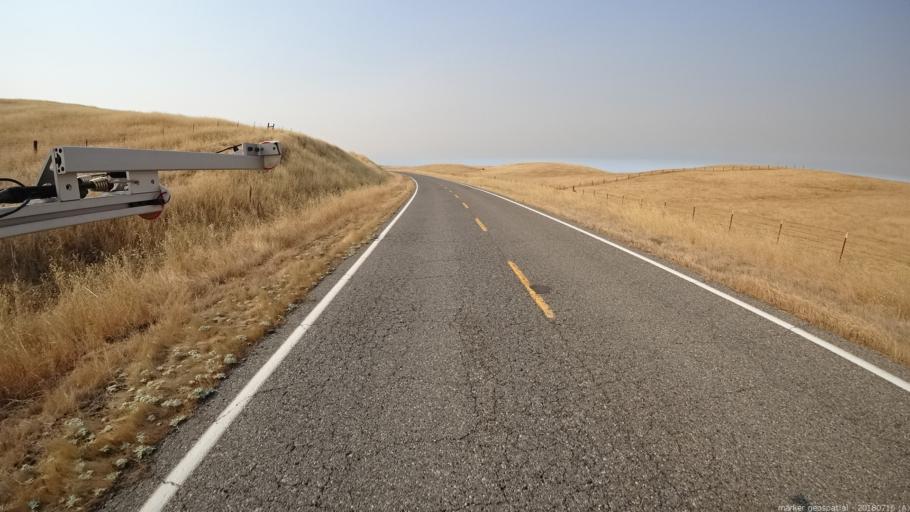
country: US
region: California
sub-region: Madera County
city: Madera Acres
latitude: 37.1743
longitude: -120.0041
